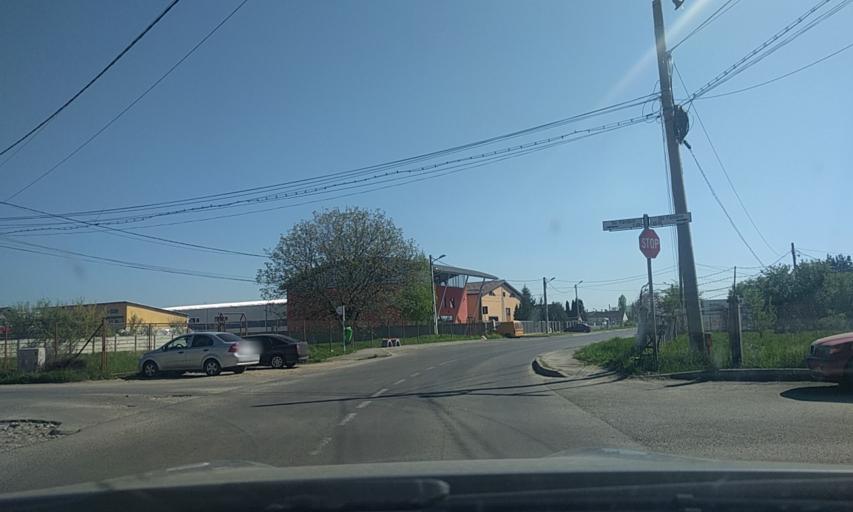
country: RO
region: Brasov
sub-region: Comuna Bod
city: Colonia Bod
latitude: 45.7075
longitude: 25.5755
